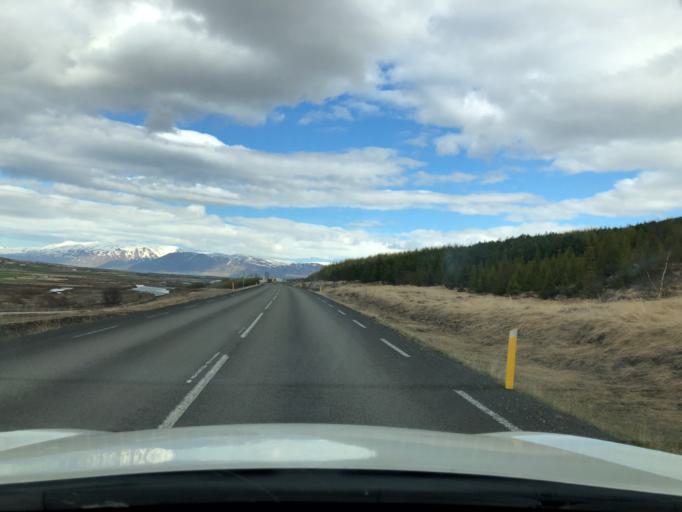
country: IS
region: Northeast
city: Akureyri
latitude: 65.7375
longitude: -18.2913
